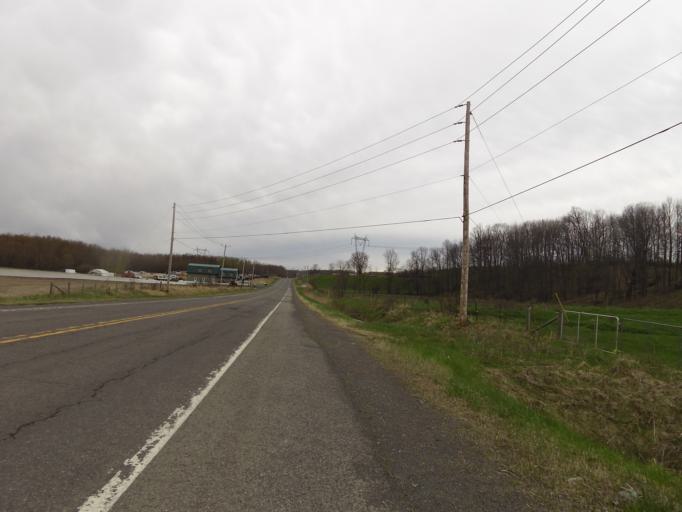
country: CA
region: Quebec
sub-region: Monteregie
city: Rigaud
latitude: 45.5373
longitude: -74.3127
